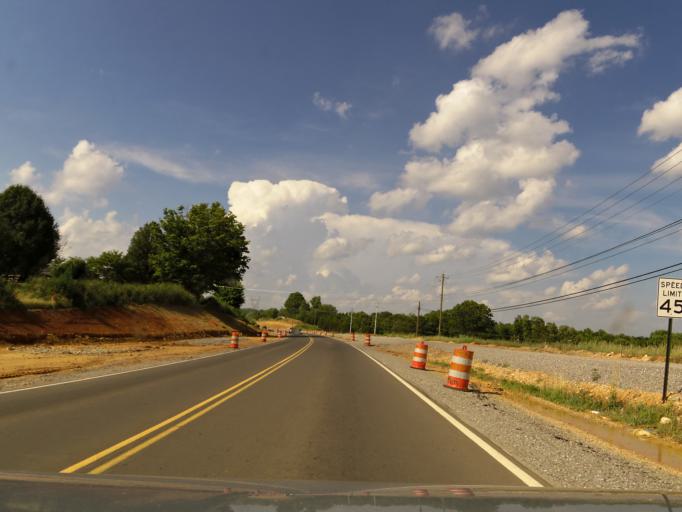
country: US
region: Tennessee
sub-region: Knox County
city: Knoxville
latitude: 36.1010
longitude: -83.9109
